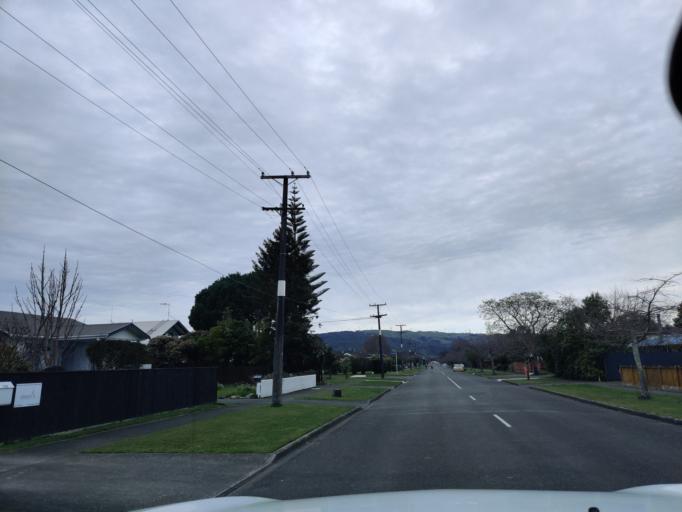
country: NZ
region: Manawatu-Wanganui
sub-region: Palmerston North City
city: Palmerston North
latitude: -40.2880
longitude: 175.7506
